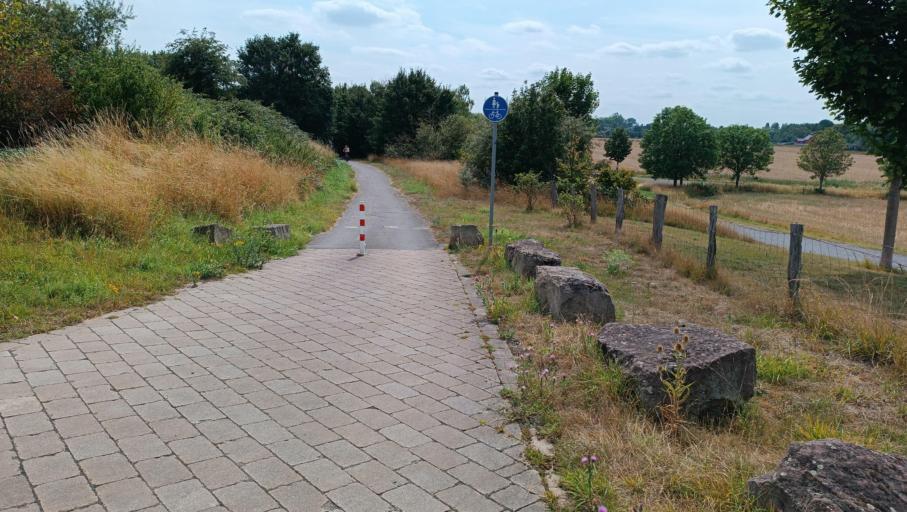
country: DE
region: North Rhine-Westphalia
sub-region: Regierungsbezirk Dusseldorf
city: Hochfeld
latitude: 51.4288
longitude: 6.7099
